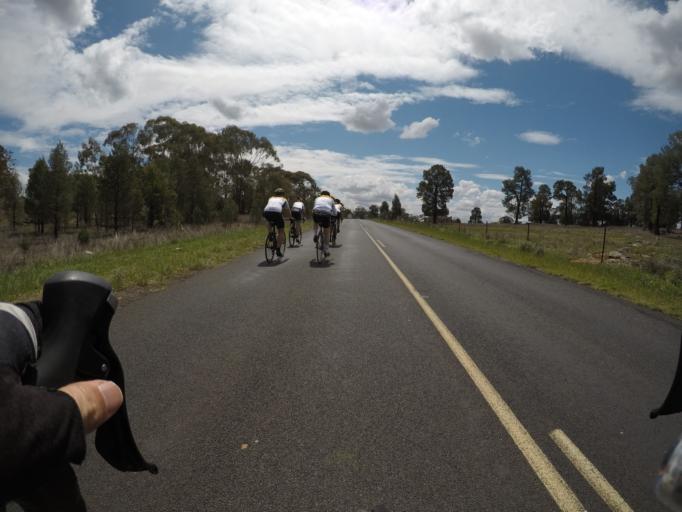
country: AU
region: New South Wales
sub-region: Dubbo Municipality
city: Dubbo
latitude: -32.2892
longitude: 148.5981
